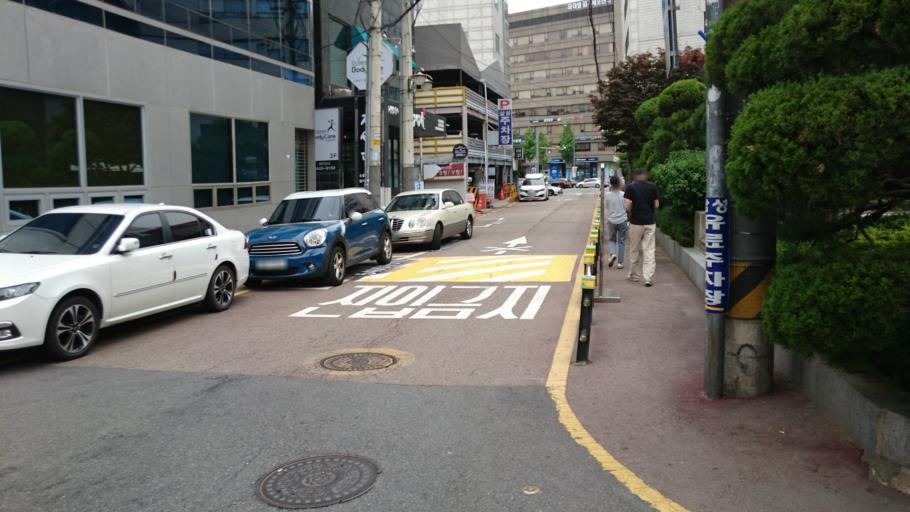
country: KR
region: Seoul
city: Seoul
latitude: 37.5282
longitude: 127.0326
